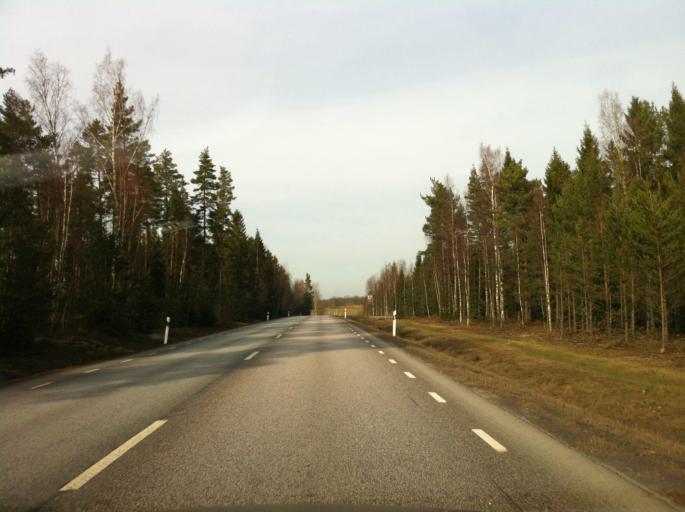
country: SE
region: Vaestra Goetaland
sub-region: Mariestads Kommun
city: Mariestad
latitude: 58.7842
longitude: 13.9660
